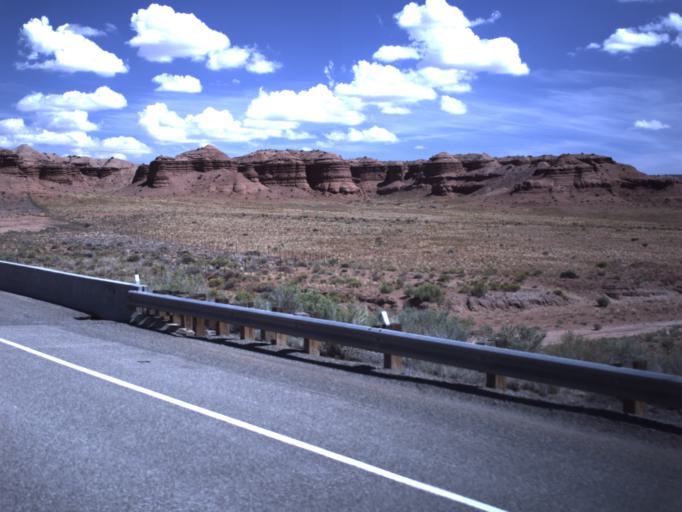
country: US
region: Utah
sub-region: Emery County
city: Ferron
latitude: 38.8438
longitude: -111.0612
